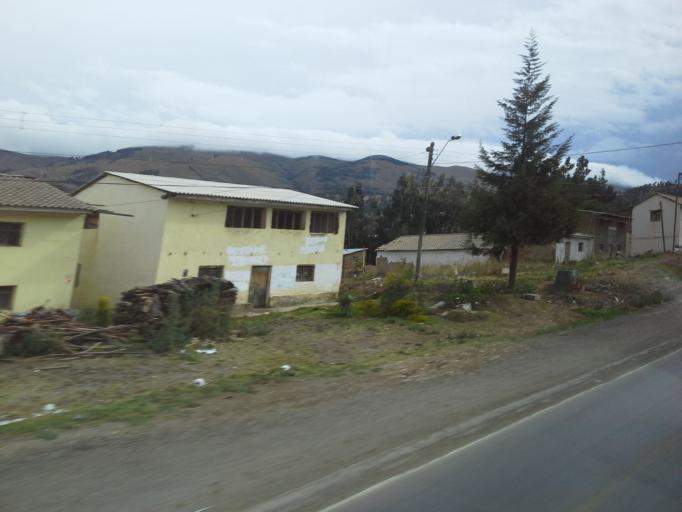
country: BO
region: Cochabamba
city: Colomi
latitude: -17.4200
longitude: -65.9478
